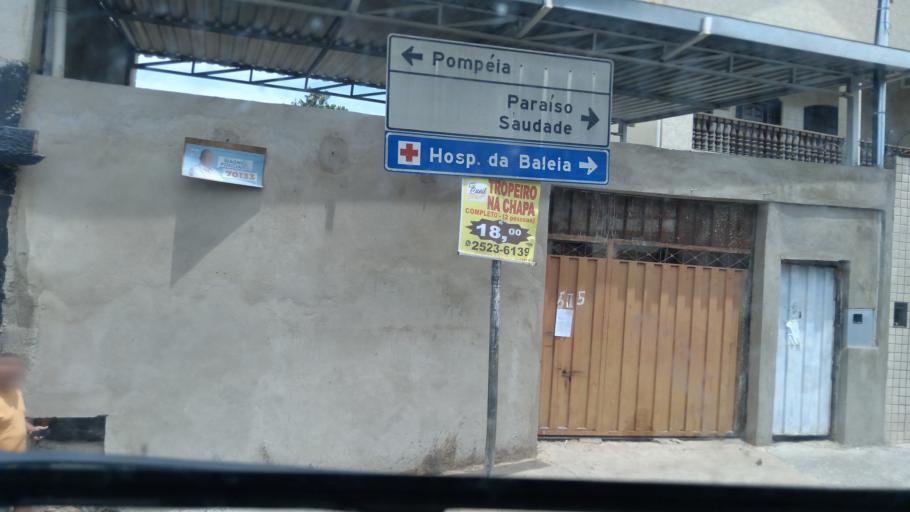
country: BR
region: Minas Gerais
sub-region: Belo Horizonte
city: Belo Horizonte
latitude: -19.9153
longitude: -43.9053
